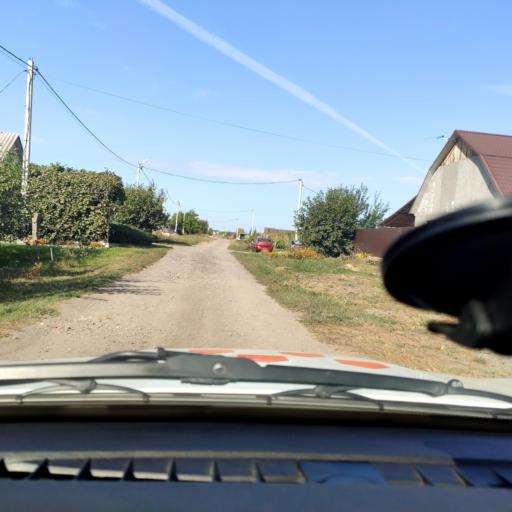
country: RU
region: Voronezj
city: Podkletnoye
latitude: 51.6042
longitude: 39.4286
